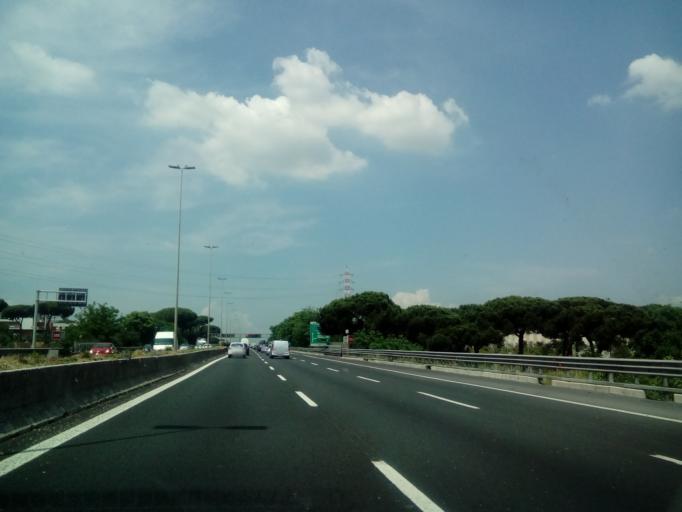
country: IT
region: Latium
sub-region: Citta metropolitana di Roma Capitale
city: Setteville
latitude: 41.9034
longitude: 12.6155
